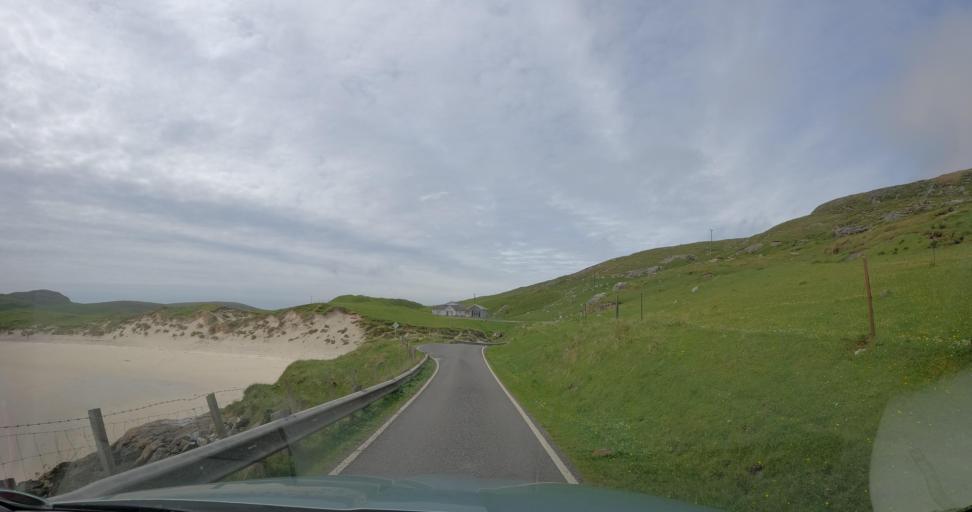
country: GB
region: Scotland
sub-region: Eilean Siar
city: Barra
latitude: 56.9271
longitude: -7.5335
